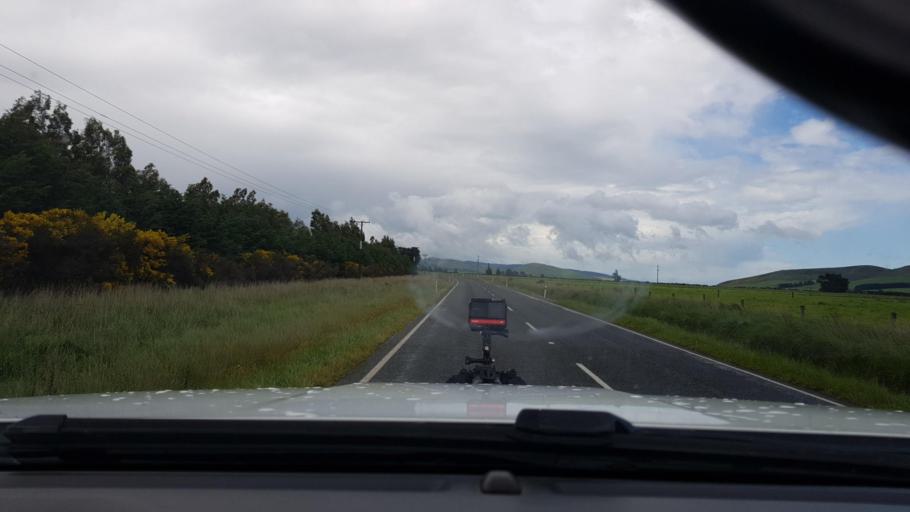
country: NZ
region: Southland
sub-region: Southland District
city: Winton
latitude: -45.7386
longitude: 168.3960
